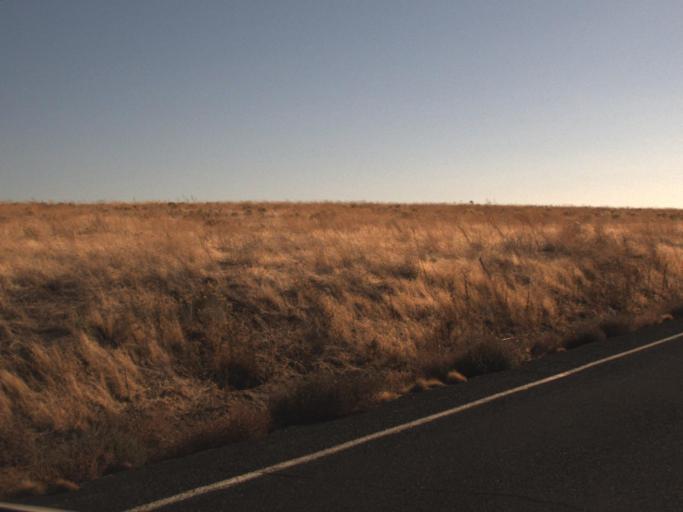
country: US
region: Washington
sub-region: Adams County
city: Ritzville
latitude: 47.0573
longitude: -118.6630
